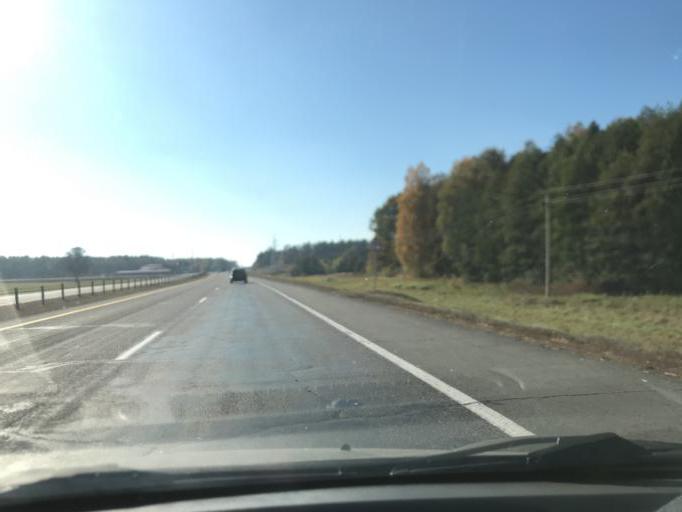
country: BY
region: Gomel
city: Horad Rechytsa
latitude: 52.3361
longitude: 30.5477
